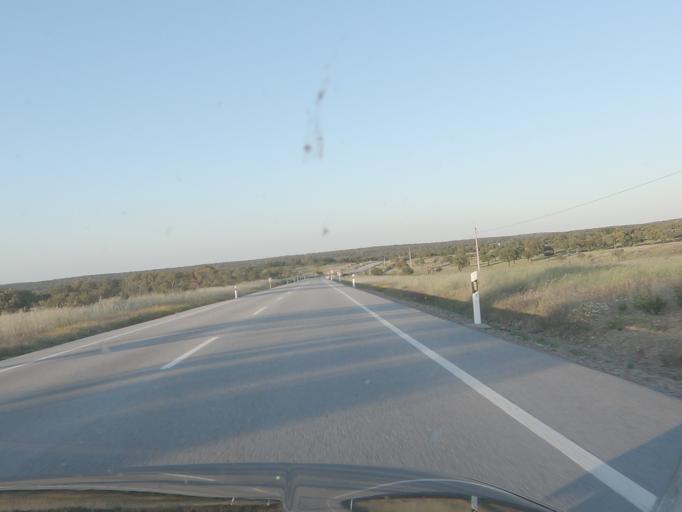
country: ES
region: Extremadura
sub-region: Provincia de Caceres
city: Carbajo
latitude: 39.5012
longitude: -7.1715
